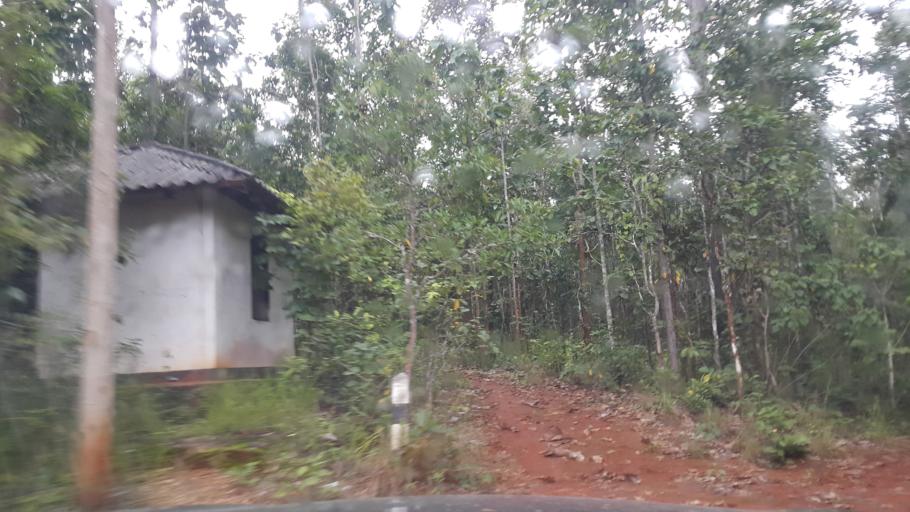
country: TH
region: Chiang Mai
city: San Sai
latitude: 18.9991
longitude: 99.1341
